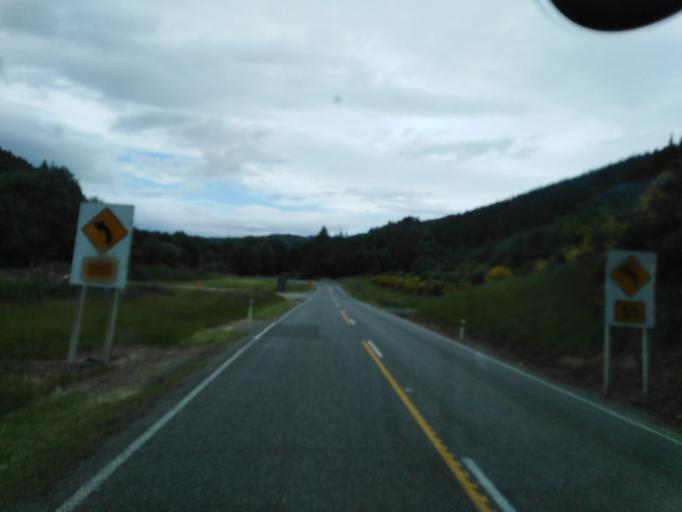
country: NZ
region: Tasman
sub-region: Tasman District
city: Wakefield
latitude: -41.4849
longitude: 172.8876
